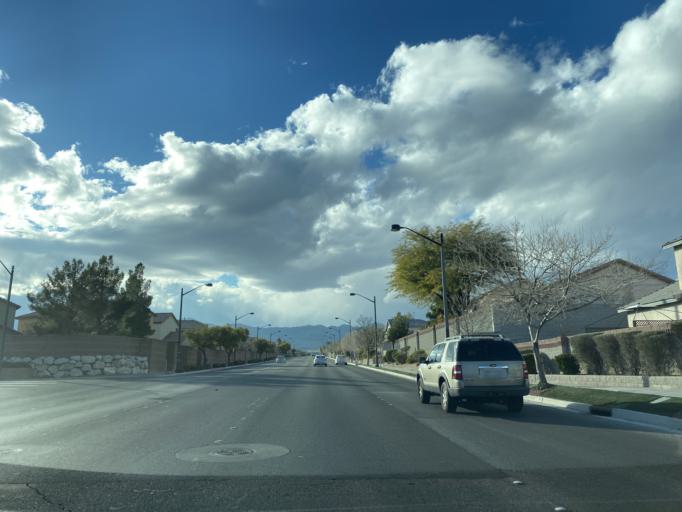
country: US
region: Nevada
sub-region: Clark County
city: Summerlin South
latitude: 36.2846
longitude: -115.2921
